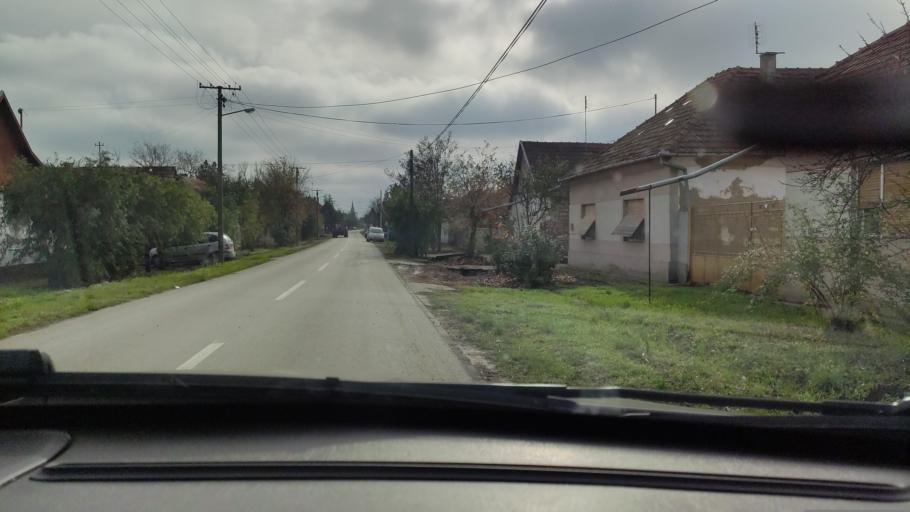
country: RS
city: Jazovo
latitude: 45.9016
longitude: 20.2168
